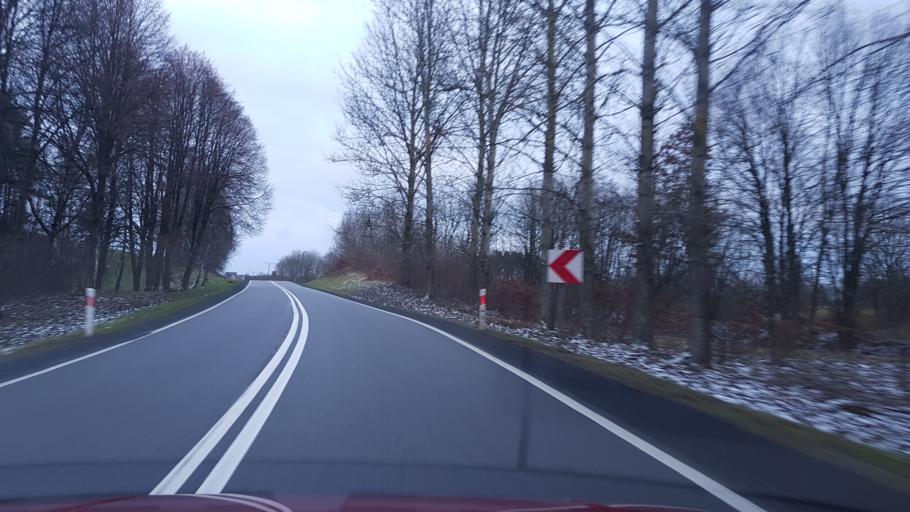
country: PL
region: Pomeranian Voivodeship
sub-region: Powiat bytowski
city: Tuchomie
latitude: 54.0493
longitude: 17.2250
